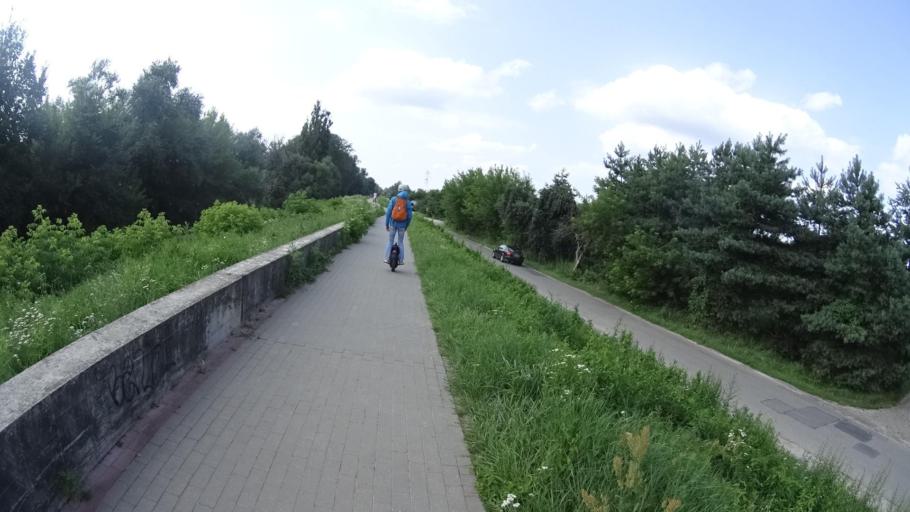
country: PL
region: Masovian Voivodeship
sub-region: Powiat legionowski
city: Jablonna
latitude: 52.3434
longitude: 20.9272
